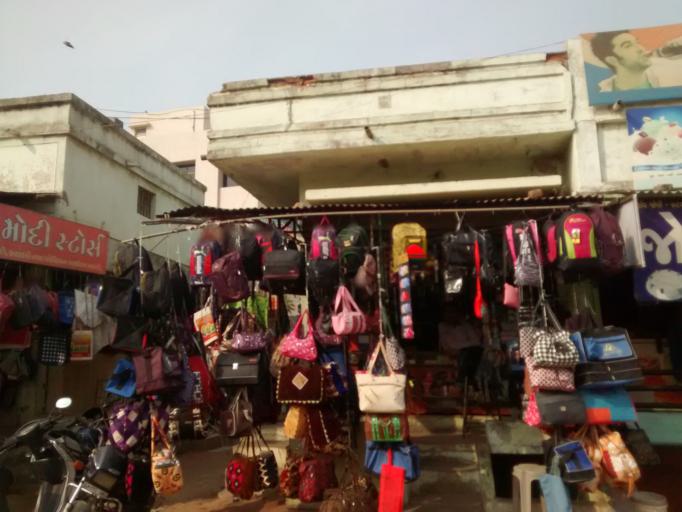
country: IN
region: Gujarat
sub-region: Gandhinagar
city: Dahegam
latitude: 23.1696
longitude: 72.8213
